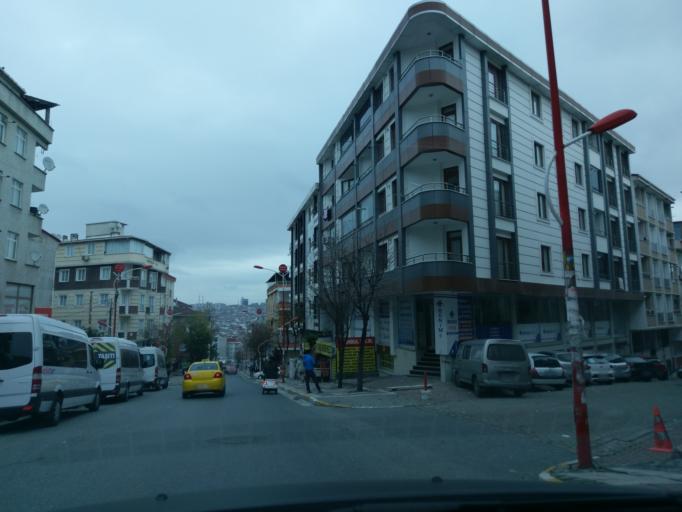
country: TR
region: Istanbul
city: Esenyurt
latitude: 41.0162
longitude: 28.6635
